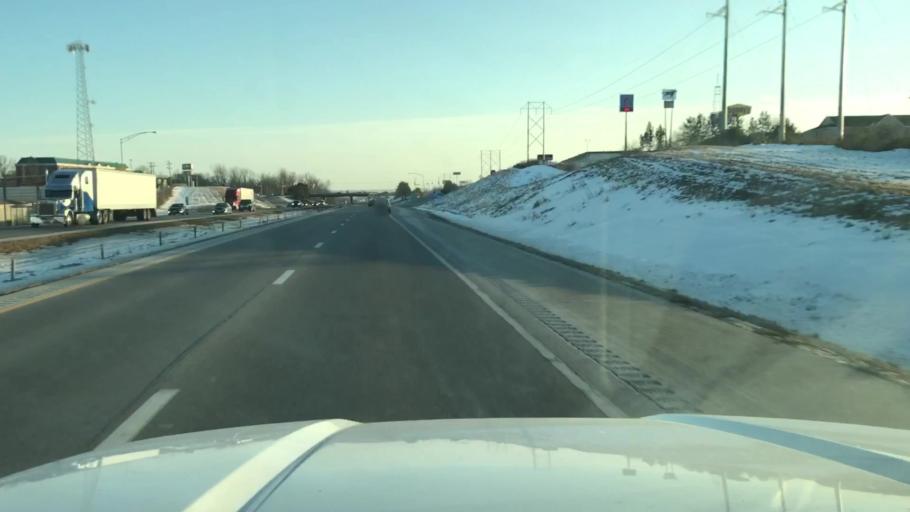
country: US
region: Missouri
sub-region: Buchanan County
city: Saint Joseph
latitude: 39.7817
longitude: -94.7945
